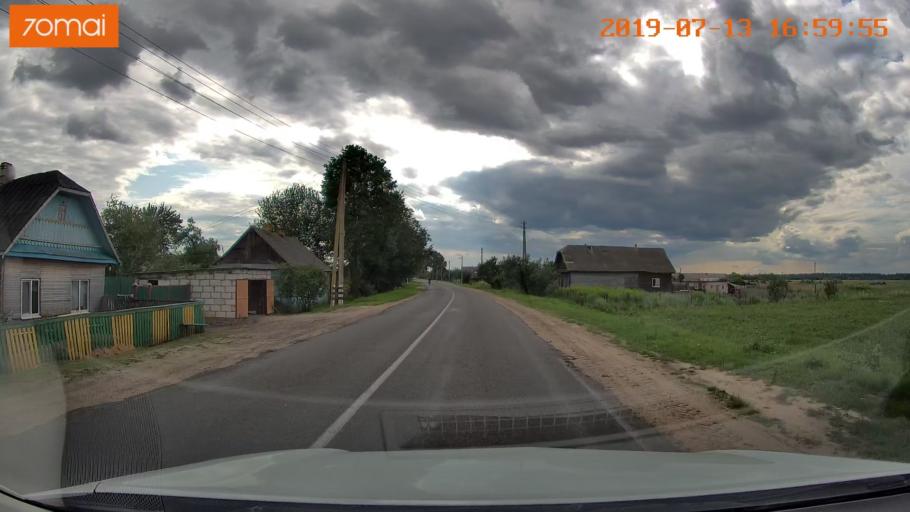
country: BY
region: Mogilev
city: Kirawsk
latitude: 53.2963
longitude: 29.4212
